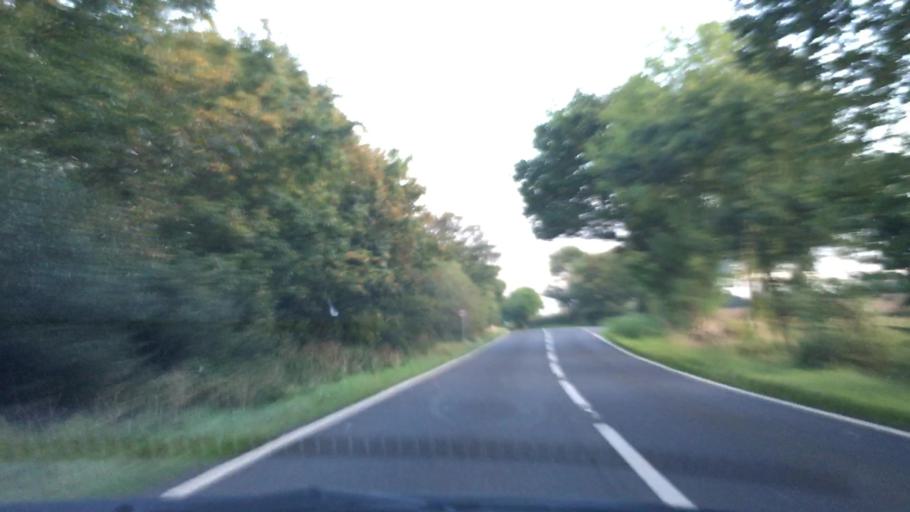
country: GB
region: England
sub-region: North East Lincolnshire
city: Wold Newton
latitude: 53.4779
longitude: -0.1192
